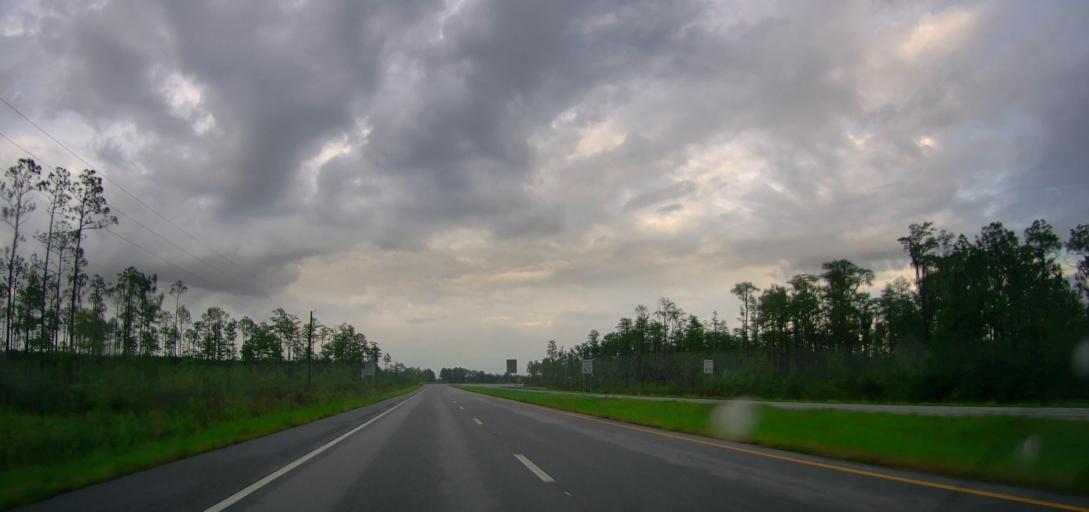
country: US
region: Georgia
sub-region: Ware County
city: Deenwood
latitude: 31.1508
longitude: -82.4582
